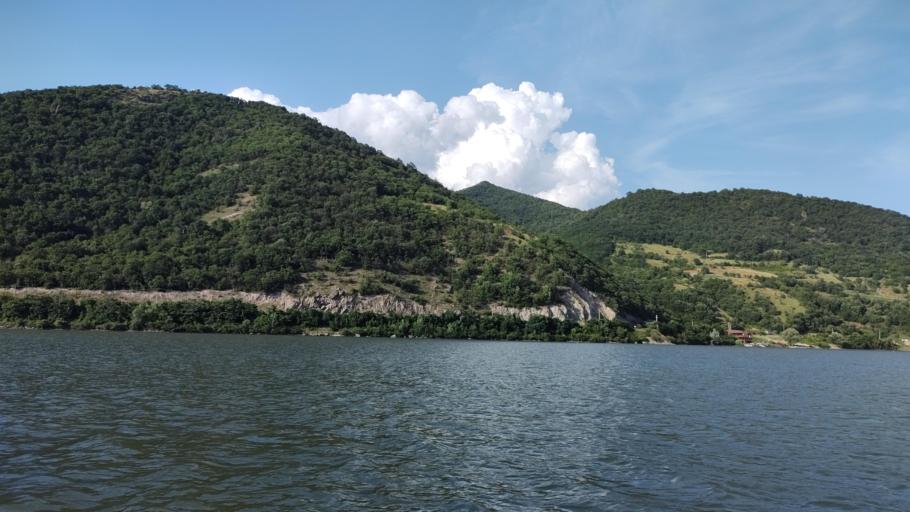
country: RO
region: Mehedinti
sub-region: Comuna Svinita
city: Svinita
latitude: 44.5411
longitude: 22.0509
